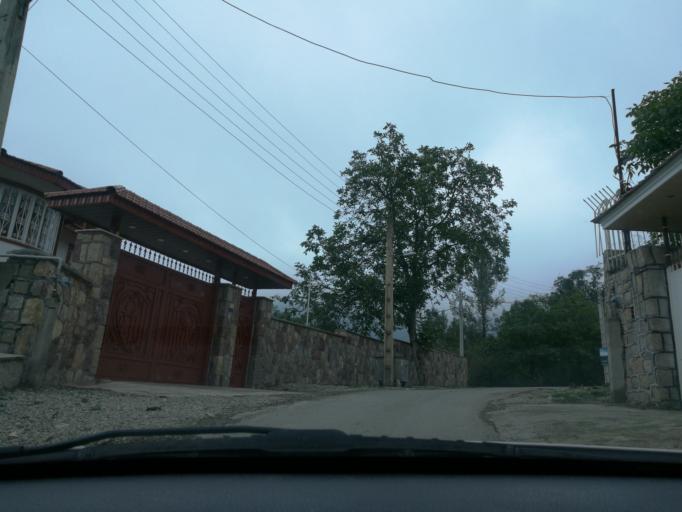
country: IR
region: Mazandaran
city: `Abbasabad
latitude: 36.4973
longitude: 51.2088
